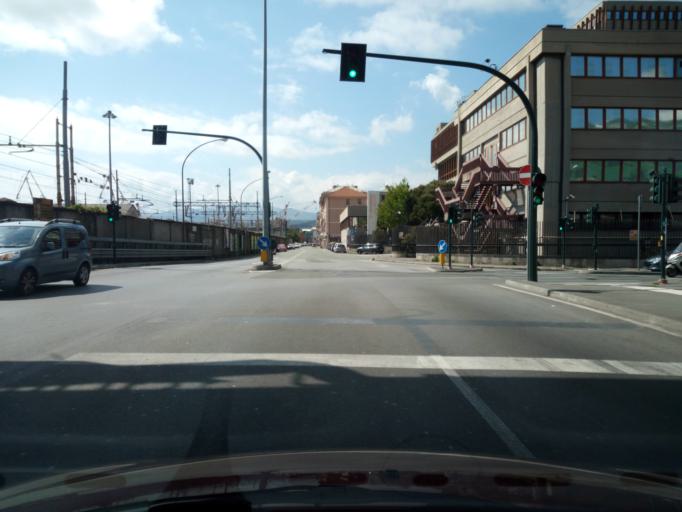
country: IT
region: Liguria
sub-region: Provincia di Genova
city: San Teodoro
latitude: 44.4215
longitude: 8.8524
